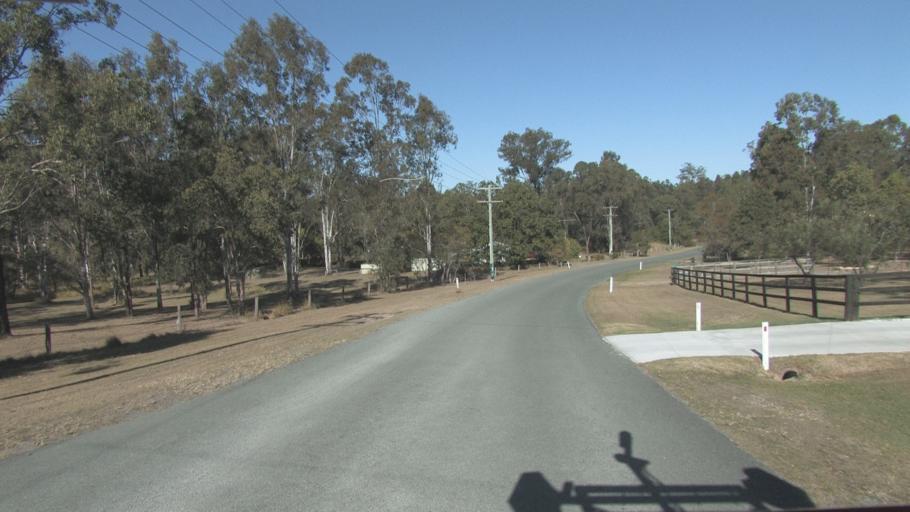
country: AU
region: Queensland
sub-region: Logan
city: Cedar Vale
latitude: -27.8288
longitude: 153.0446
